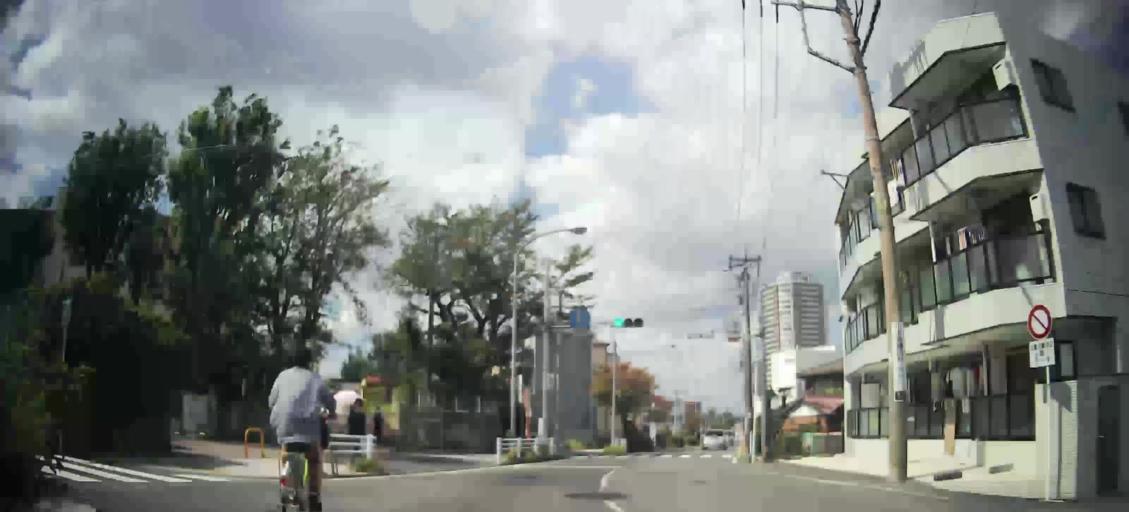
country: JP
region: Kanagawa
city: Yokohama
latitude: 35.4722
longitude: 139.5528
